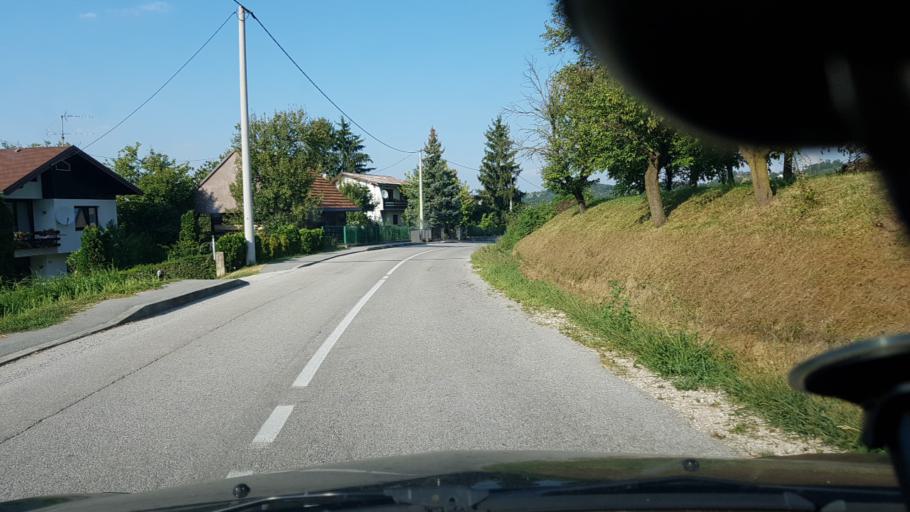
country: HR
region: Zagrebacka
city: Bregana
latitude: 45.9130
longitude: 15.6985
